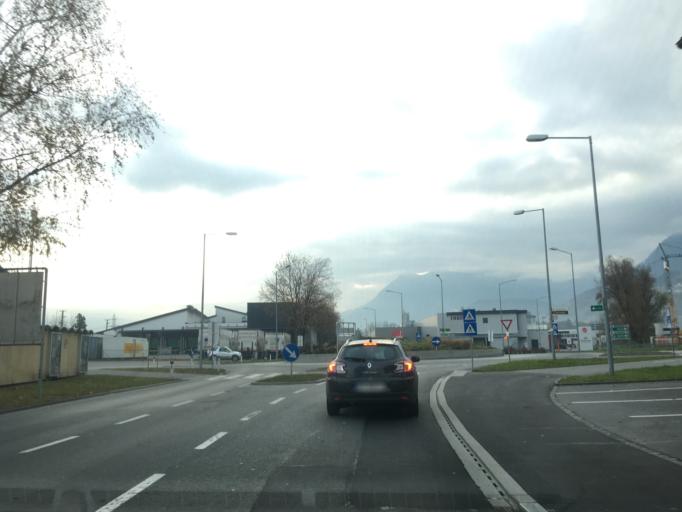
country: AT
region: Vorarlberg
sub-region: Politischer Bezirk Feldkirch
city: Gofis
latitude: 47.2199
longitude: 9.6377
